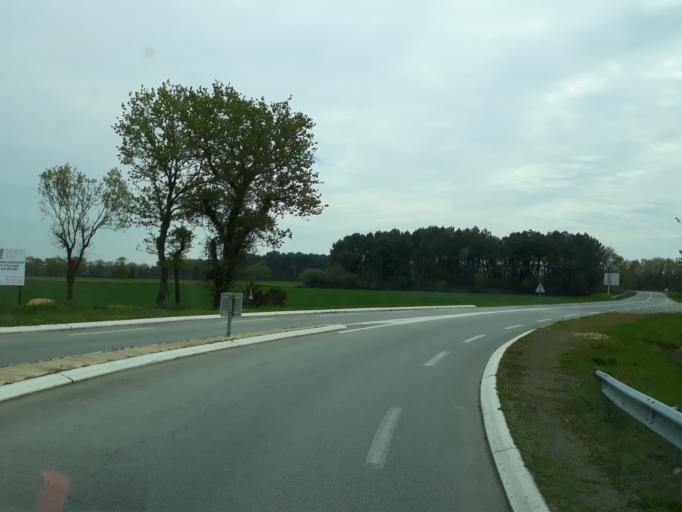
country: FR
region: Brittany
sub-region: Departement du Morbihan
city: Peaule
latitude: 47.5347
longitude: -2.3956
